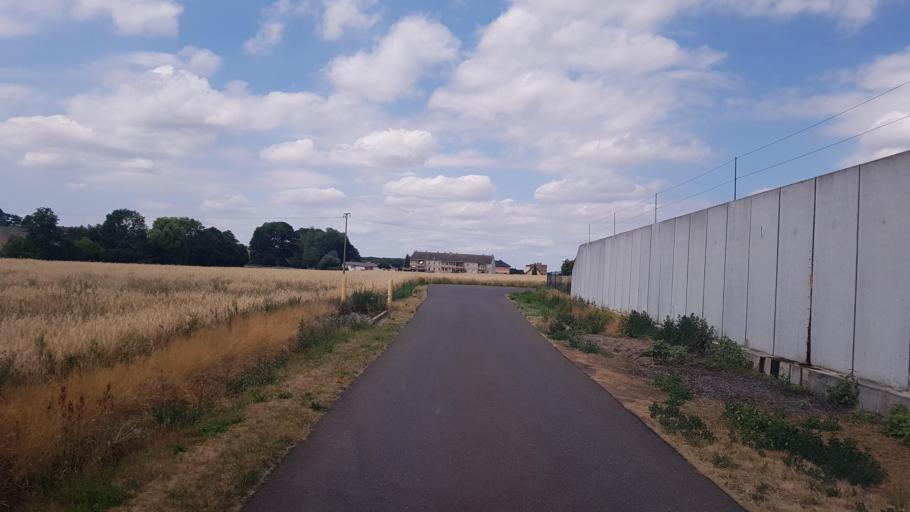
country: DE
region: Brandenburg
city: Juterbog
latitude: 51.9652
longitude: 13.0495
